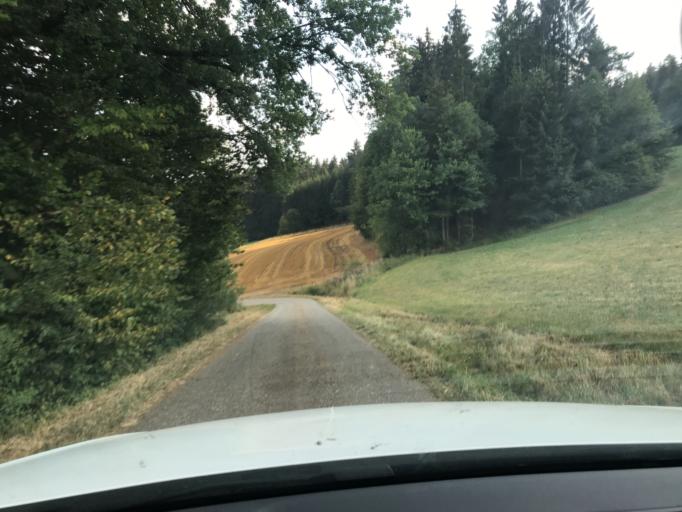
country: DE
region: Bavaria
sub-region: Upper Franconia
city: Pegnitz
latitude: 49.7464
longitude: 11.6025
